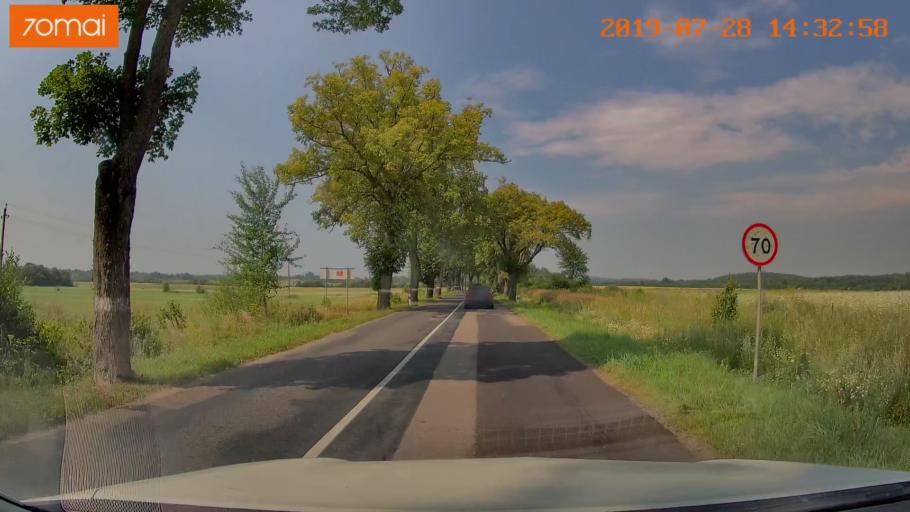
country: RU
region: Kaliningrad
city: Primorsk
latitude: 54.8162
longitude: 20.0364
